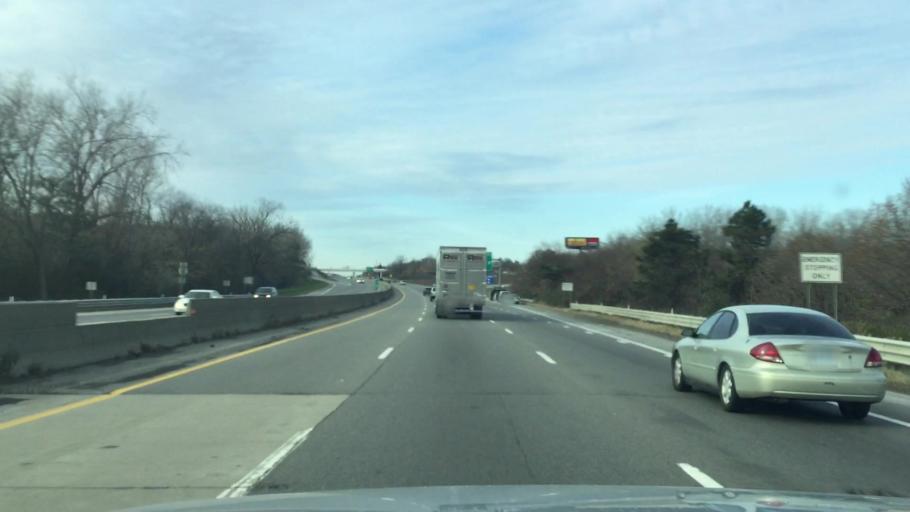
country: US
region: Michigan
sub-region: Washtenaw County
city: Ypsilanti
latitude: 42.2310
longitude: -83.6076
